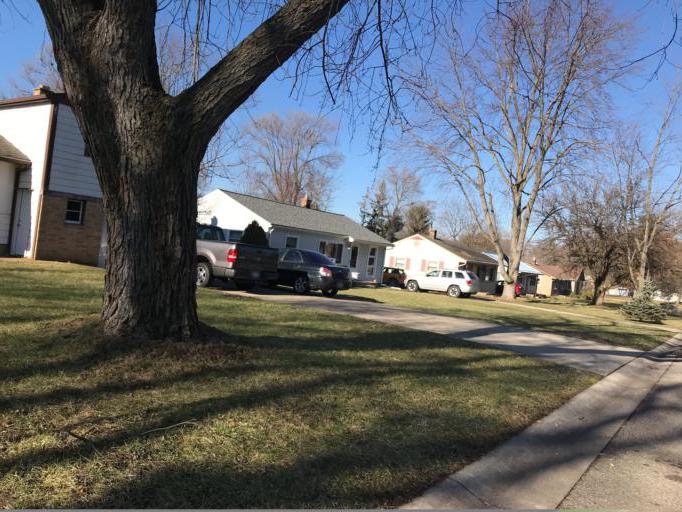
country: US
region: Michigan
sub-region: Washtenaw County
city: Ann Arbor
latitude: 42.2417
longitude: -83.7185
